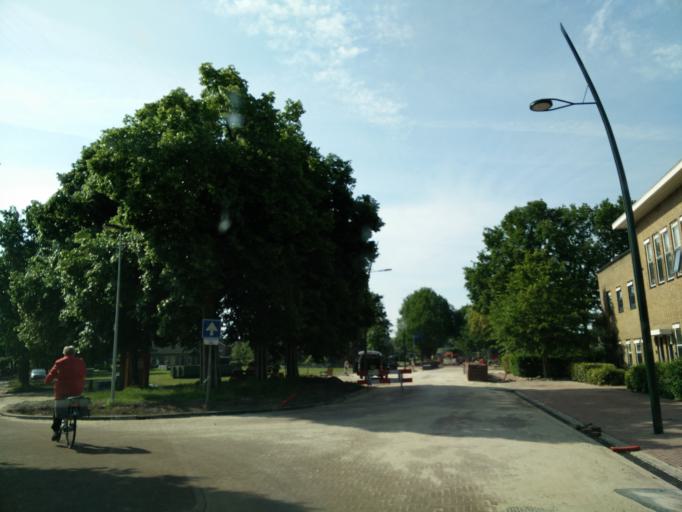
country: NL
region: Drenthe
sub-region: Gemeente Aa en Hunze
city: Anloo
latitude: 52.9859
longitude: 6.6485
